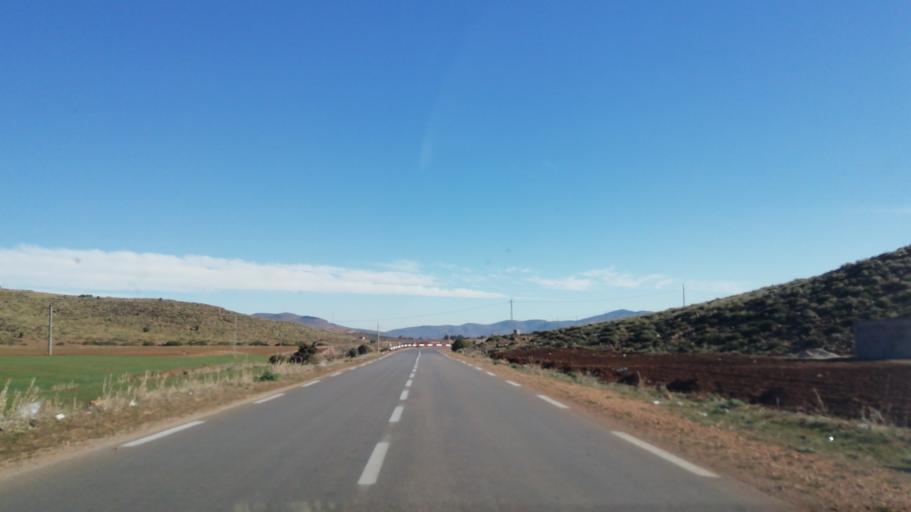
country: DZ
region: Tlemcen
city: Ouled Mimoun
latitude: 34.7743
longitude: -1.1274
